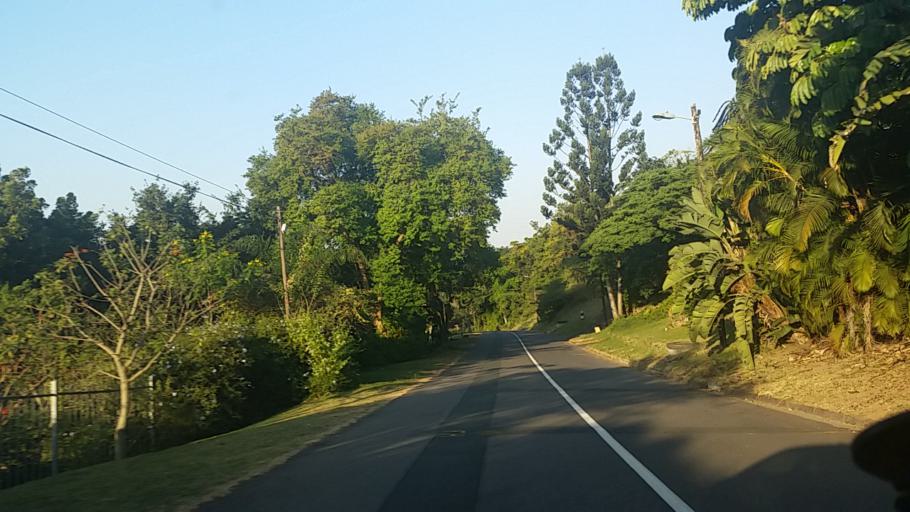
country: ZA
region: KwaZulu-Natal
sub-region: eThekwini Metropolitan Municipality
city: Berea
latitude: -29.8525
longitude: 30.9194
